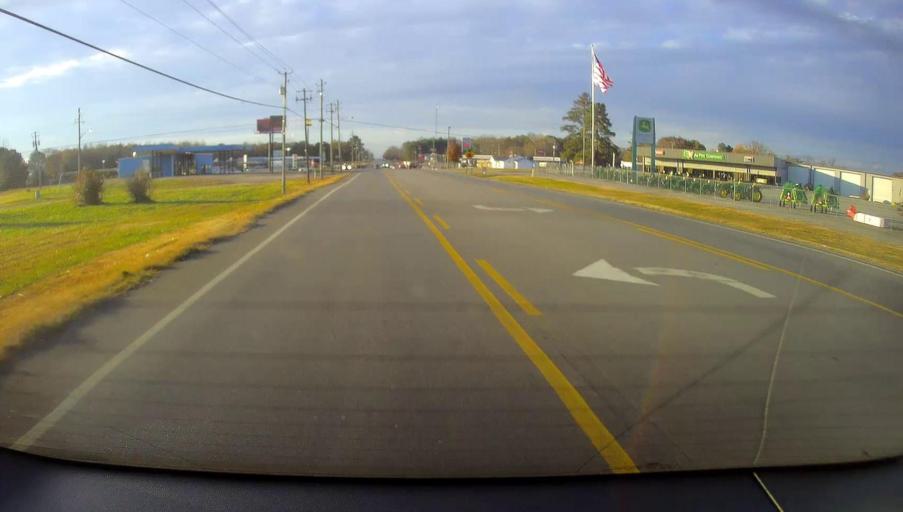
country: US
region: Alabama
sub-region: Blount County
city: Oneonta
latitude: 34.1181
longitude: -86.3928
